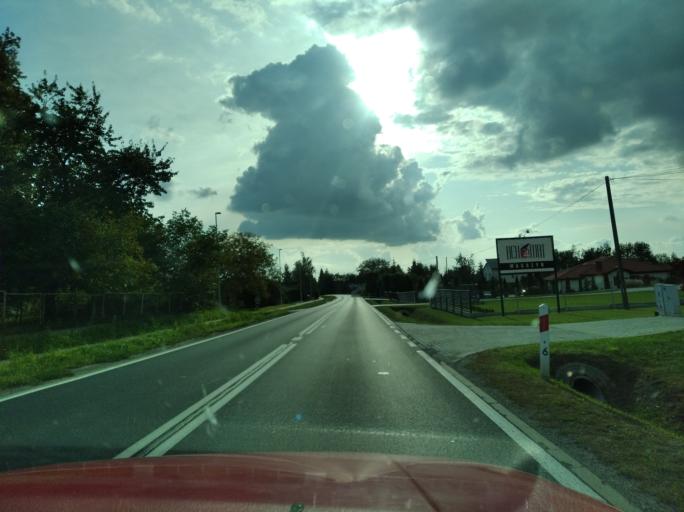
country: PL
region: Subcarpathian Voivodeship
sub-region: Powiat jaroslawski
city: Pawlosiow
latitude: 49.9831
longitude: 22.6502
